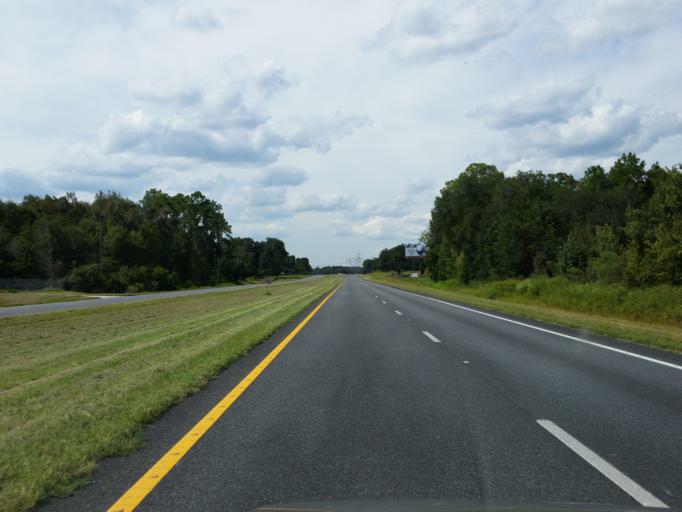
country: US
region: Florida
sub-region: Sumter County
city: Wildwood
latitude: 28.8619
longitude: -82.0755
